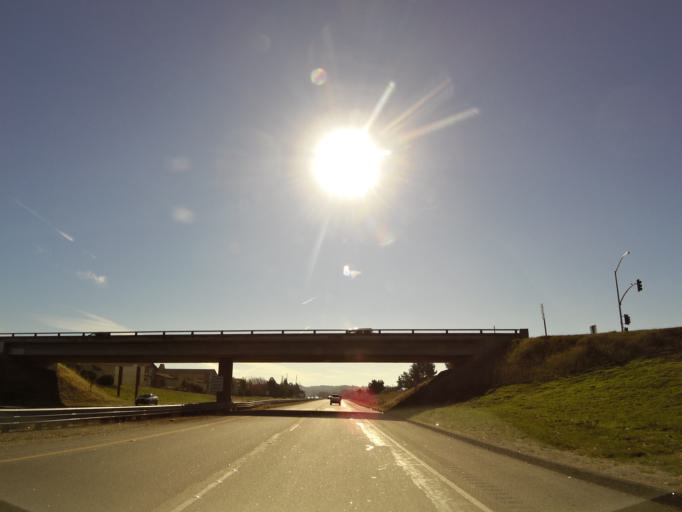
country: US
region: California
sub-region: San Luis Obispo County
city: Templeton
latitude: 35.5137
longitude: -120.6999
